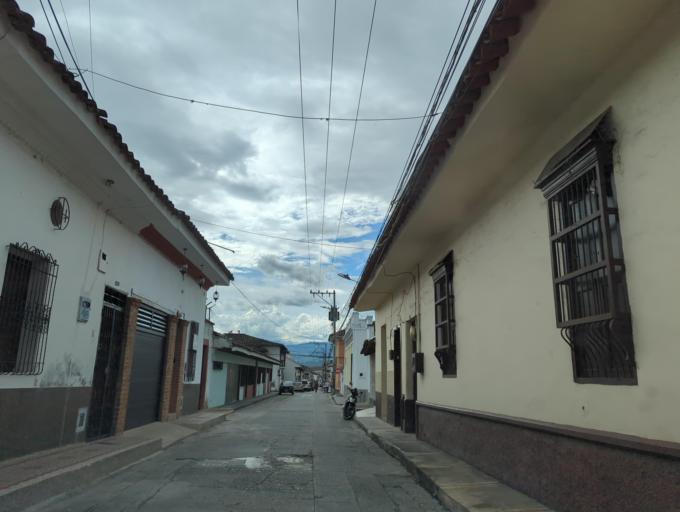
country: CO
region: Valle del Cauca
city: Buga
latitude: 3.8962
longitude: -76.3003
